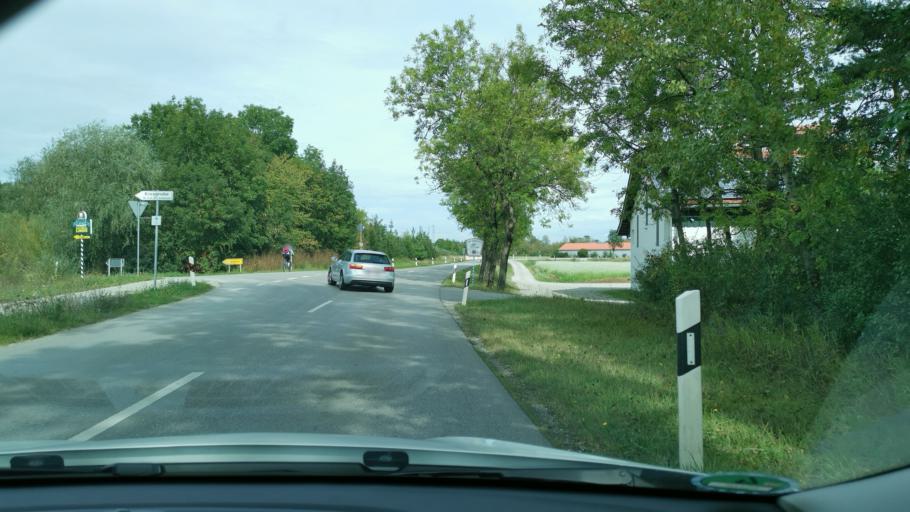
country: DE
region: Bavaria
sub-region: Upper Bavaria
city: Bergkirchen
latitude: 48.2405
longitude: 11.3583
